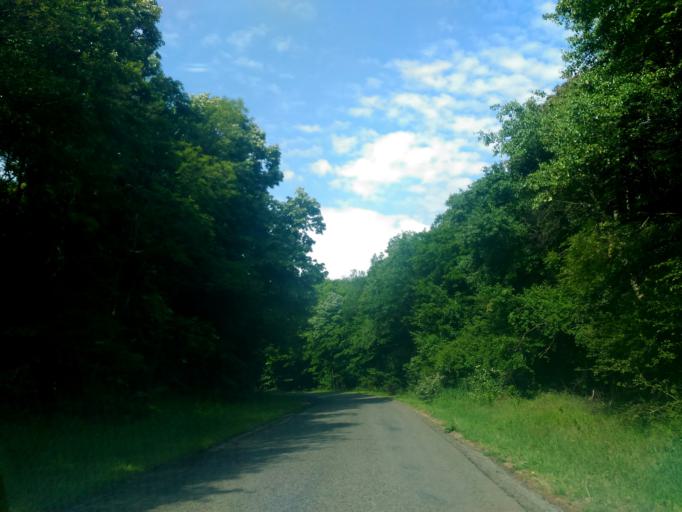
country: HU
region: Baranya
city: Pecs
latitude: 46.1231
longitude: 18.2153
